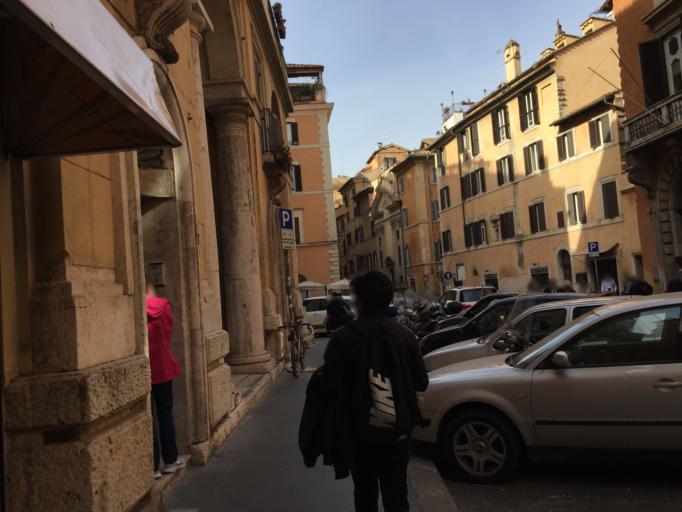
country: VA
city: Vatican City
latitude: 41.9024
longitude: 12.4775
